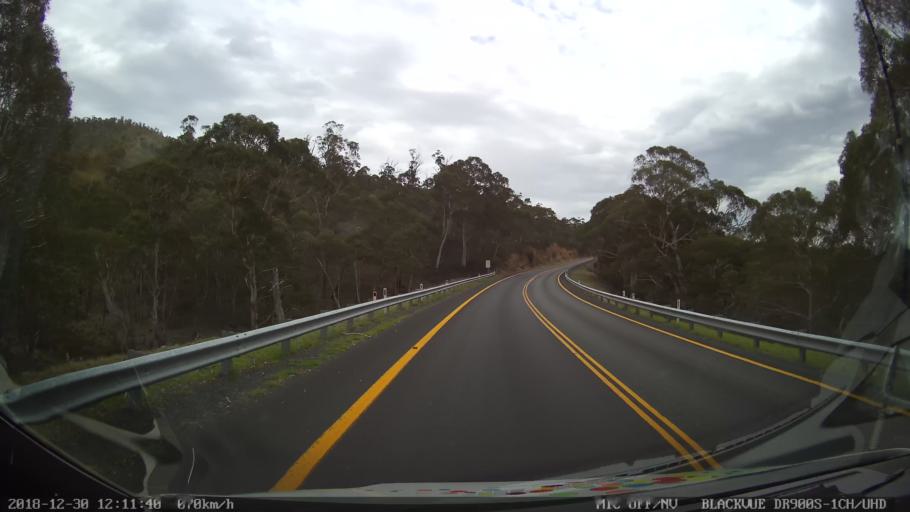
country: AU
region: New South Wales
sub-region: Snowy River
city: Jindabyne
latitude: -36.3643
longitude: 148.5868
